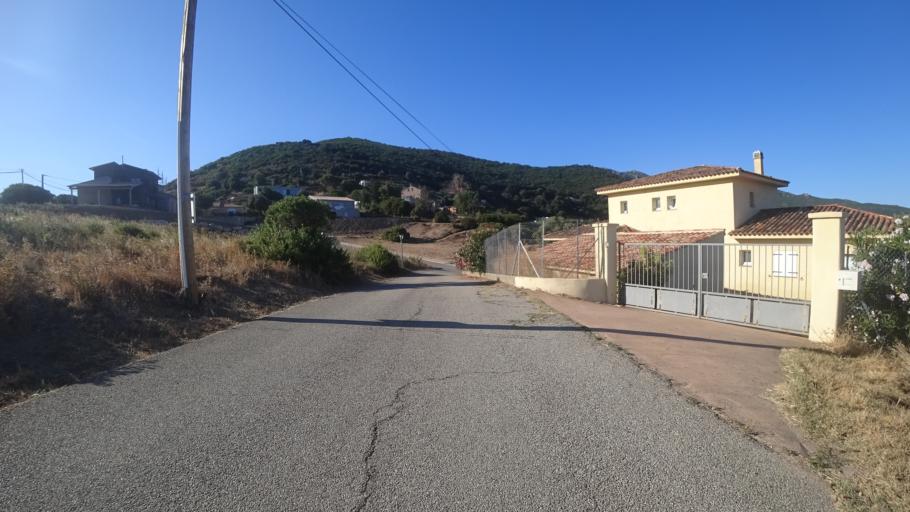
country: FR
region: Corsica
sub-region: Departement de la Corse-du-Sud
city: Alata
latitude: 41.9731
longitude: 8.6895
